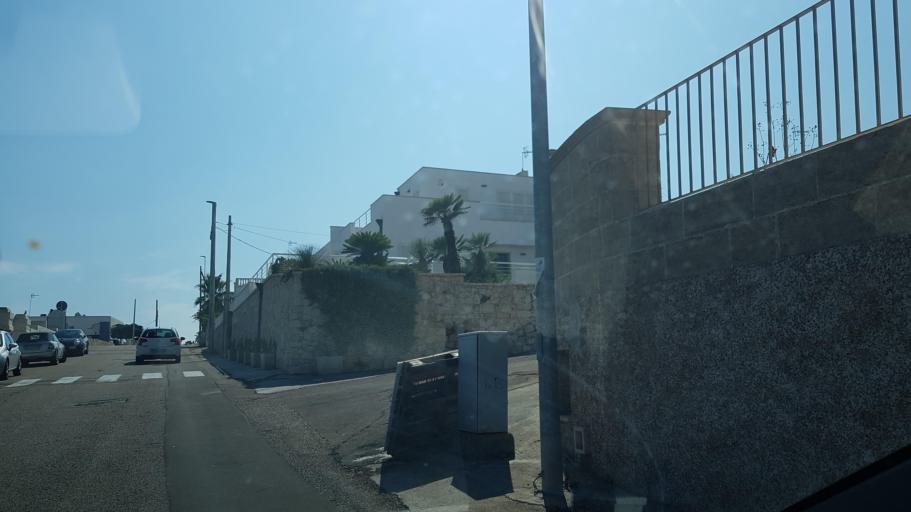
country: IT
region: Apulia
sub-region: Provincia di Lecce
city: Leuca
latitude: 39.7934
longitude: 18.3481
